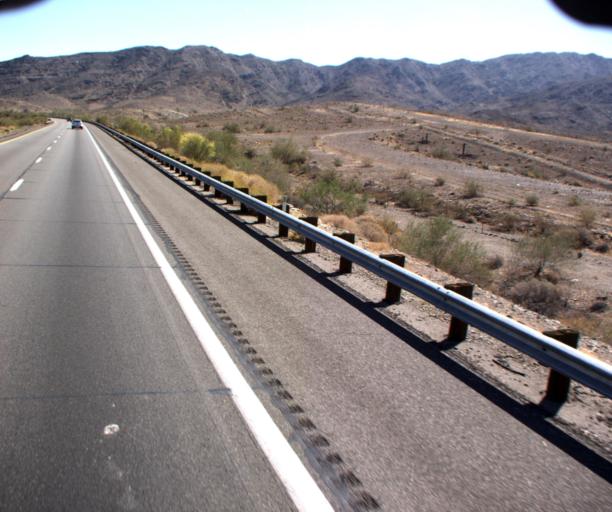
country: US
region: Arizona
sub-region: La Paz County
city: Ehrenberg
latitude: 33.6329
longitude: -114.3981
